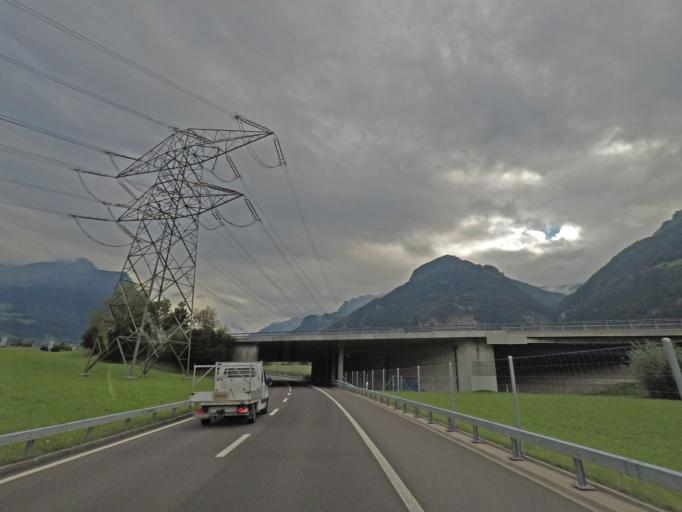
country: CH
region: Uri
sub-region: Uri
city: Seedorf
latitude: 46.8909
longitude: 8.6180
